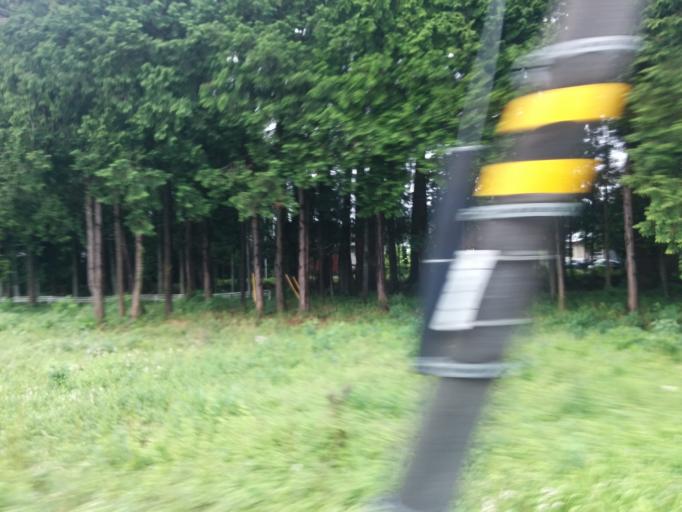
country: JP
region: Tochigi
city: Imaichi
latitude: 36.7156
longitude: 139.6954
